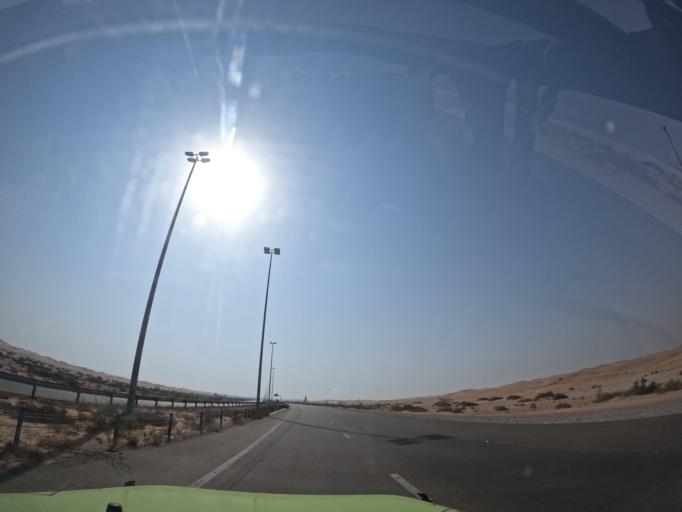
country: OM
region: Al Buraimi
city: Al Buraymi
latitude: 24.5185
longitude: 55.5560
